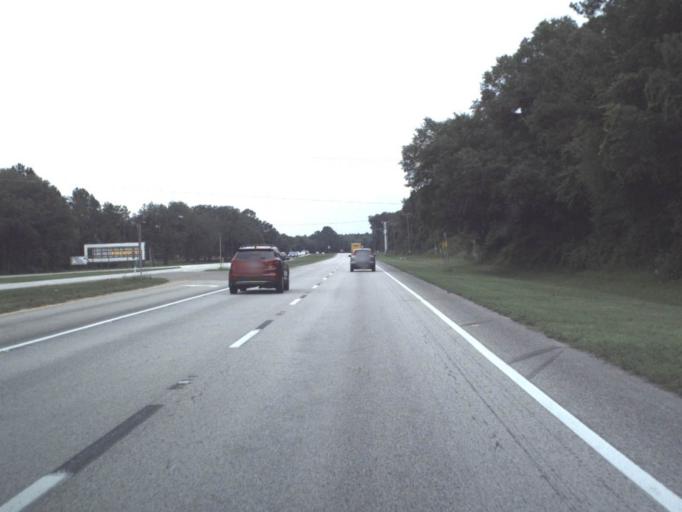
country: US
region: Florida
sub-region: Alachua County
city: Waldo
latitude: 29.8511
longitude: -82.1574
